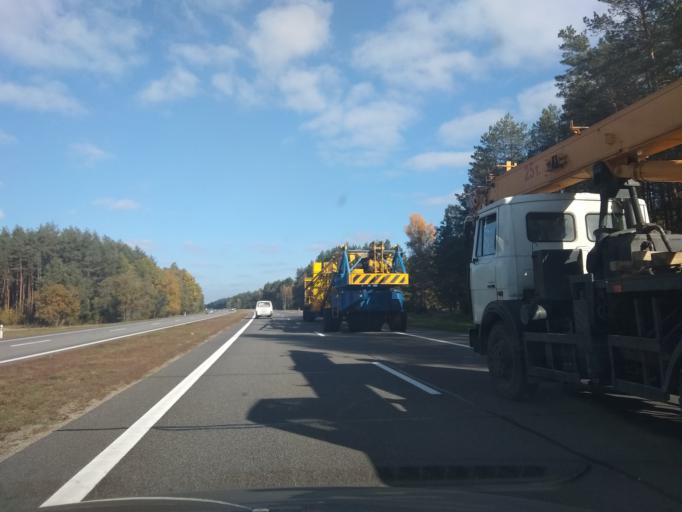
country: BY
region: Brest
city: Baranovichi
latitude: 53.0551
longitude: 25.8598
